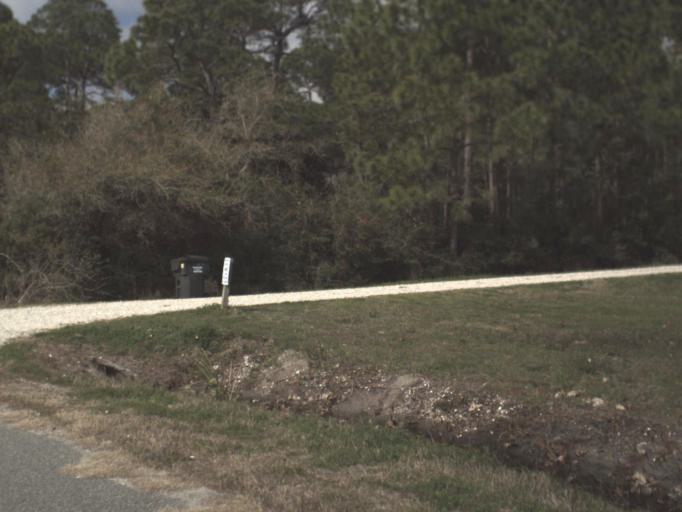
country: US
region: Florida
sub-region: Franklin County
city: Eastpoint
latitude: 29.7524
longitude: -84.8445
